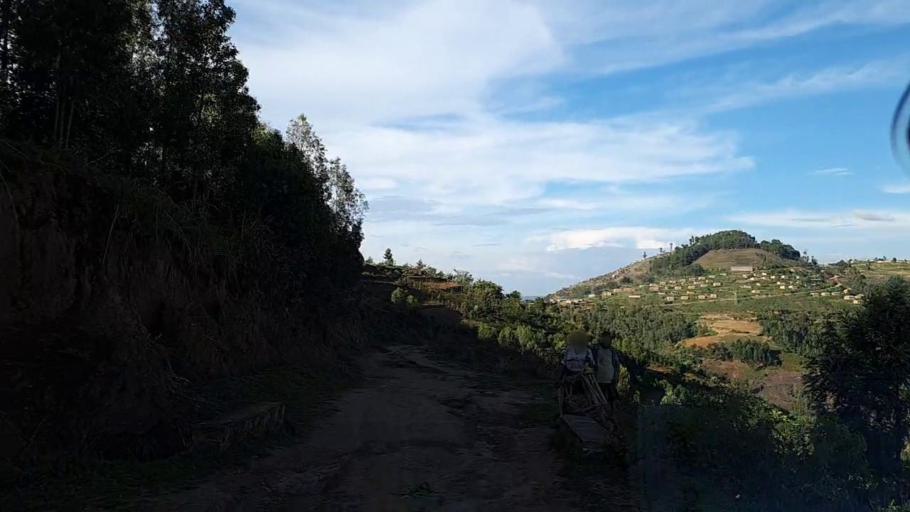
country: RW
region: Southern Province
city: Gikongoro
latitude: -2.4093
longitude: 29.5231
